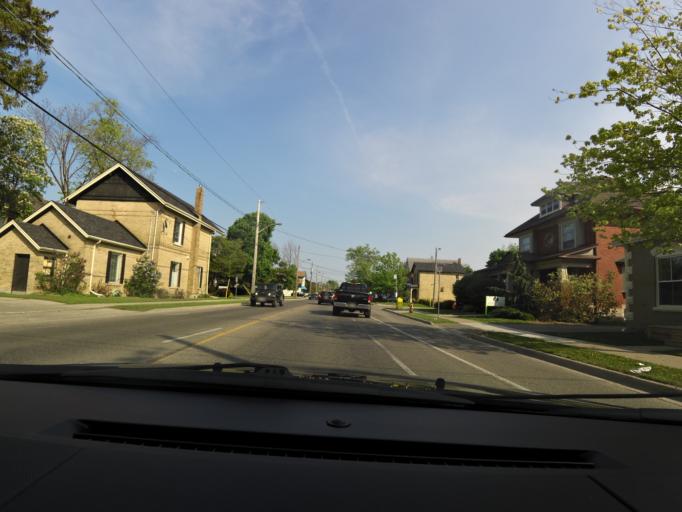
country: CA
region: Ontario
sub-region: Wellington County
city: Guelph
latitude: 43.5528
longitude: -80.2606
